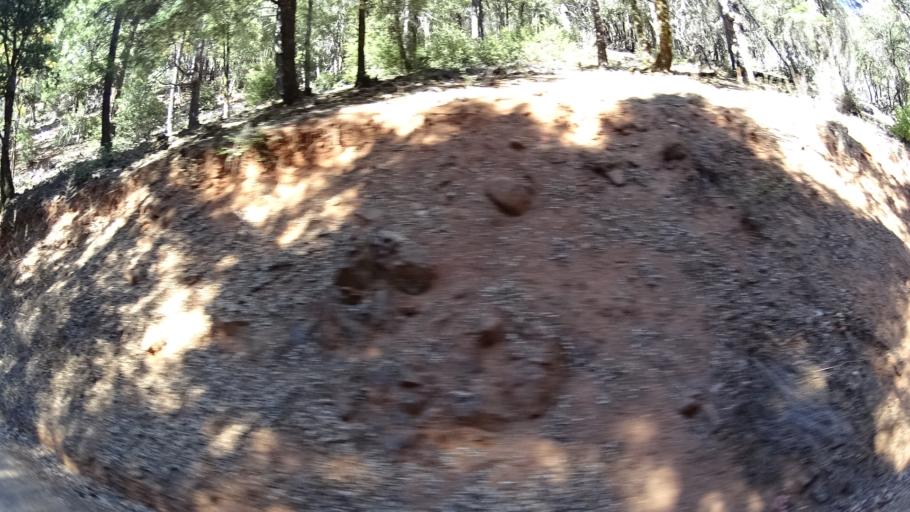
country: US
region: California
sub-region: Siskiyou County
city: Happy Camp
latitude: 41.2971
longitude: -123.1013
